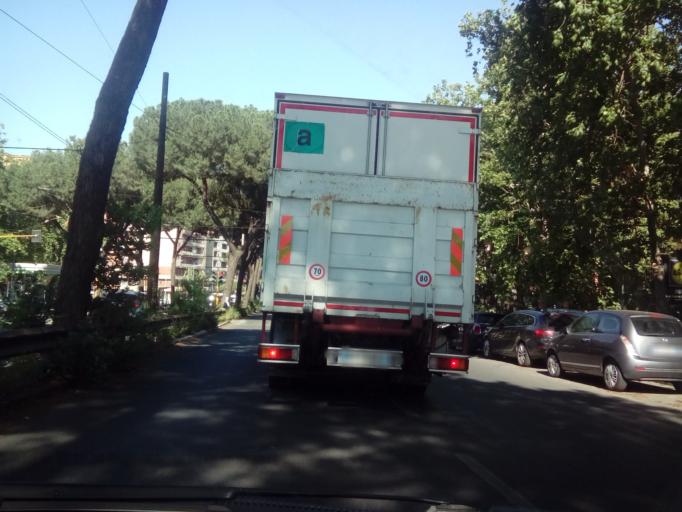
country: IT
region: Latium
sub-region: Citta metropolitana di Roma Capitale
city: Rome
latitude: 41.8945
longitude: 12.5572
